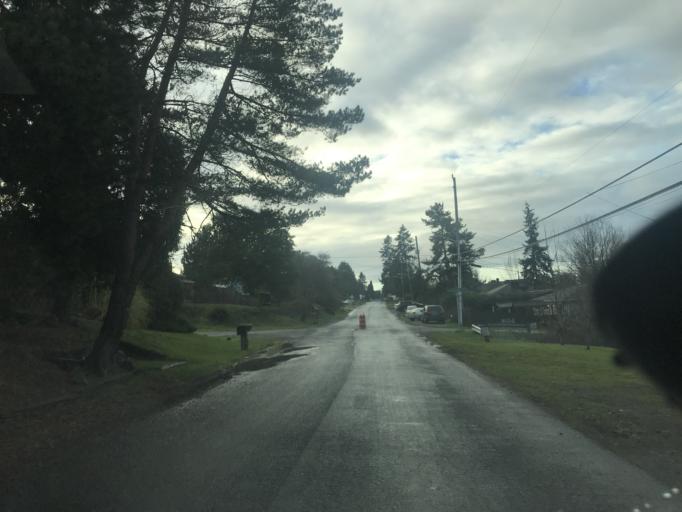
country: US
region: Washington
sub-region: King County
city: White Center
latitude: 47.5269
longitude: -122.3632
